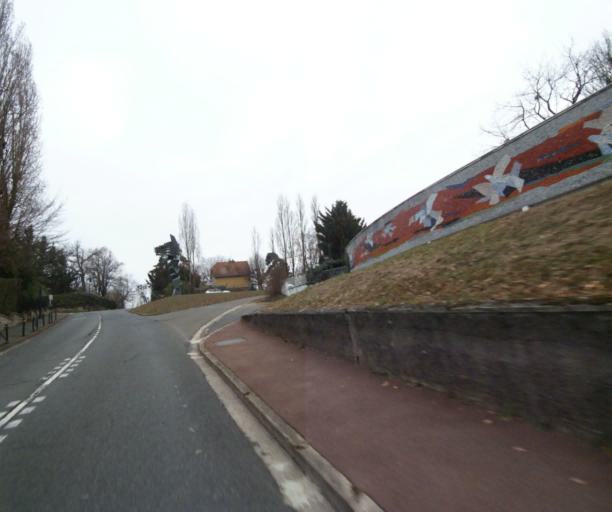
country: FR
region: Ile-de-France
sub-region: Departement des Hauts-de-Seine
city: Vaucresson
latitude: 48.8413
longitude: 2.1572
